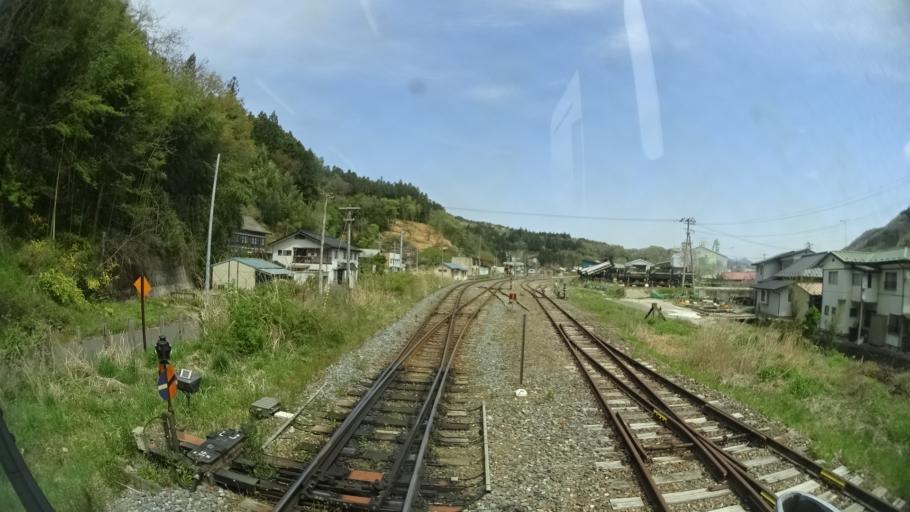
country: JP
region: Iwate
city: Ichinoseki
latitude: 38.9750
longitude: 141.2374
